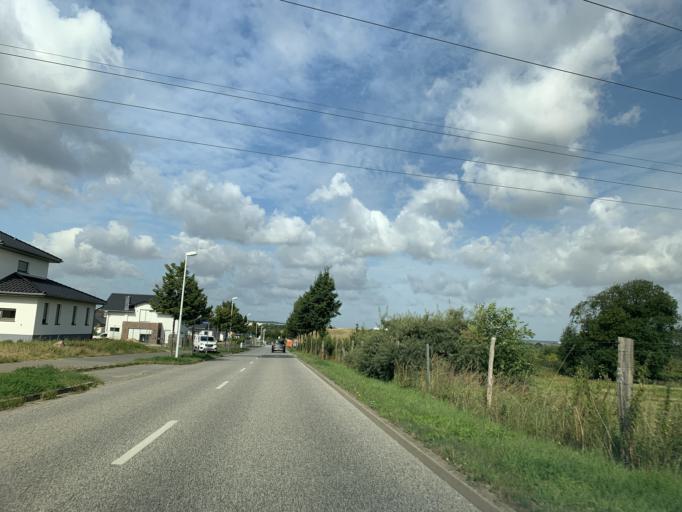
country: DE
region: Mecklenburg-Vorpommern
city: Neubrandenburg
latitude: 53.5284
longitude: 13.2806
